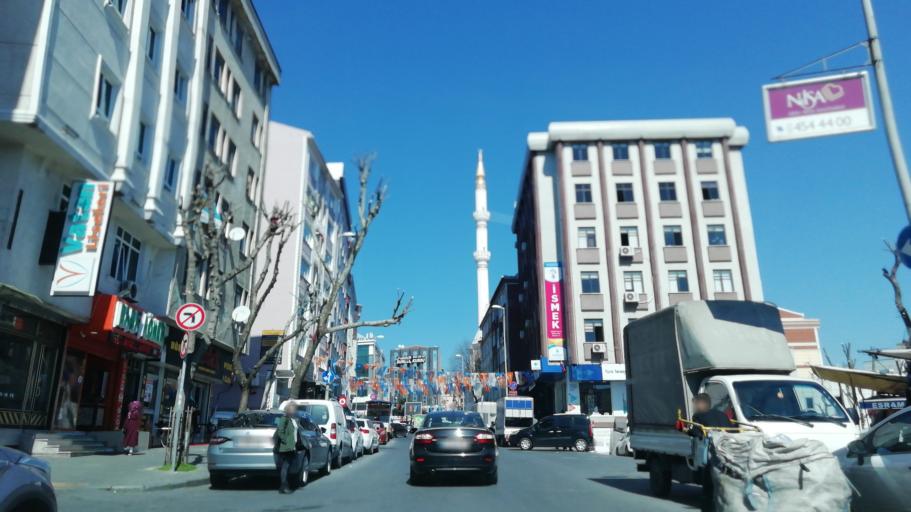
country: TR
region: Istanbul
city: Bahcelievler
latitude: 41.0013
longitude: 28.8343
